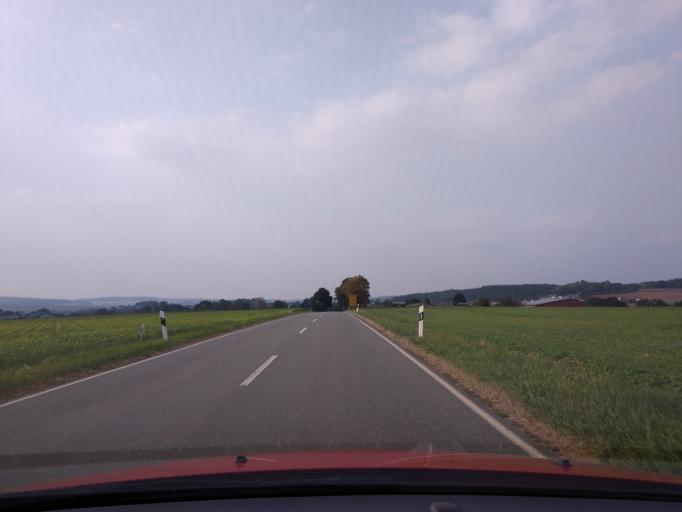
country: DE
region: Hesse
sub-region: Regierungsbezirk Kassel
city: Zierenberg
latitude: 51.4270
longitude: 9.3335
